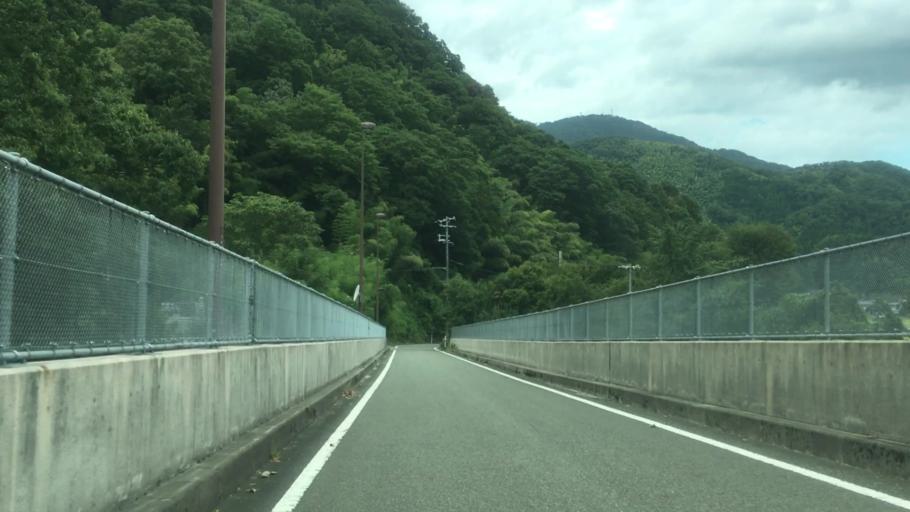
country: JP
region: Hyogo
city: Toyooka
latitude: 35.5865
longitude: 134.7991
